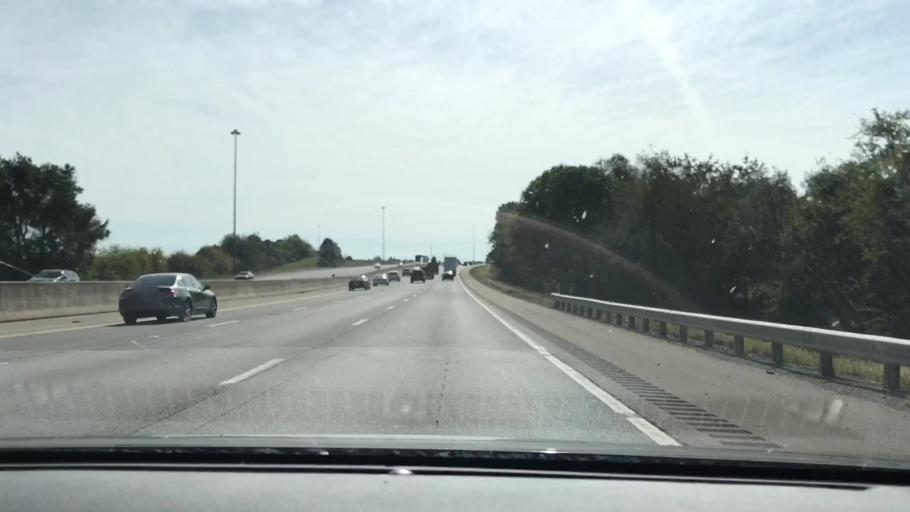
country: US
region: Kentucky
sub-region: Simpson County
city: Franklin
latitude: 36.6938
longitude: -86.5341
